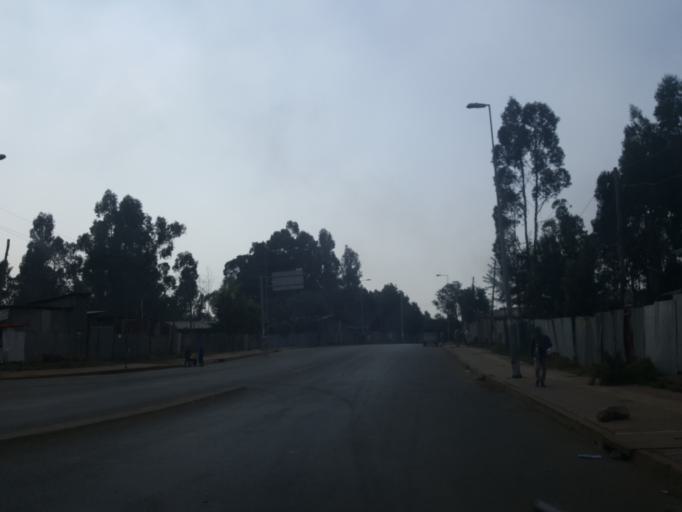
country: ET
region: Adis Abeba
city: Addis Ababa
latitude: 9.0677
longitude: 38.7212
